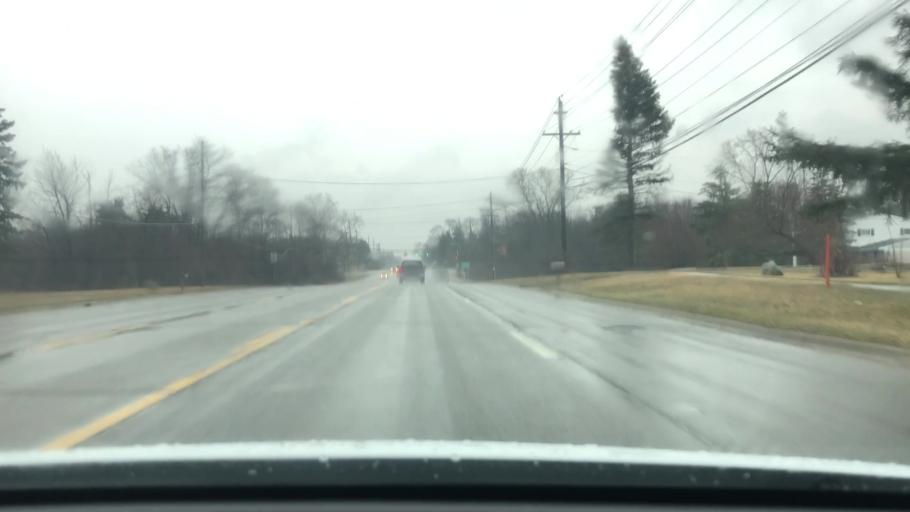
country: US
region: Michigan
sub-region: Oakland County
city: Troy
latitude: 42.5790
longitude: -83.1681
